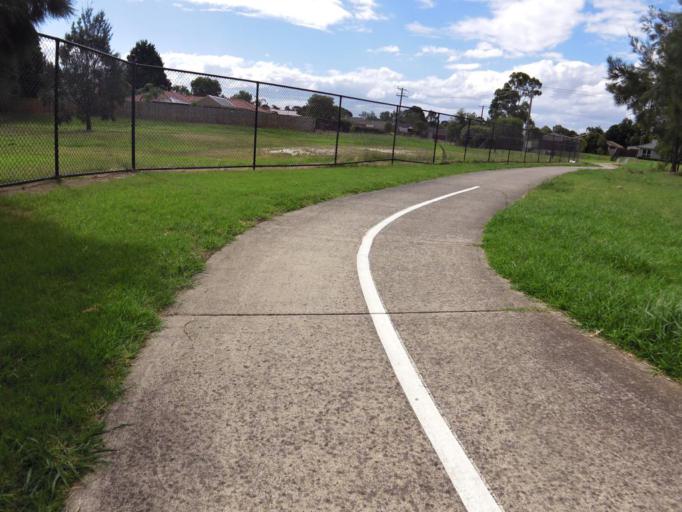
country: AU
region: Victoria
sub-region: Knox
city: Ferntree Gully
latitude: -37.8957
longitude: 145.2753
